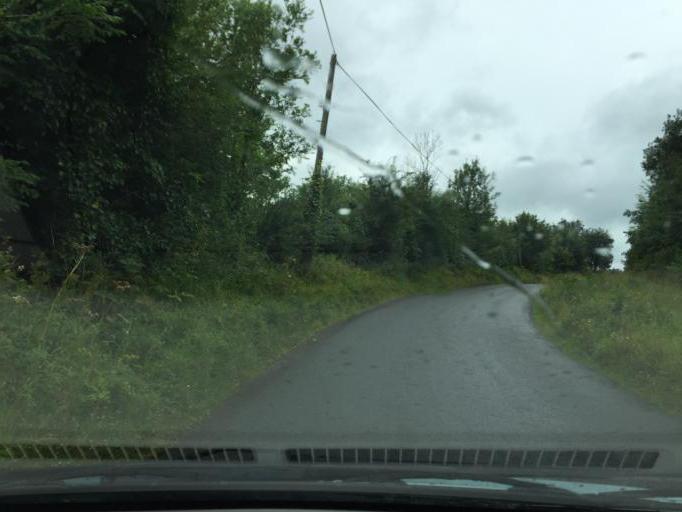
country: IE
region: Connaught
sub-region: Sligo
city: Sligo
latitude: 54.2347
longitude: -8.4524
